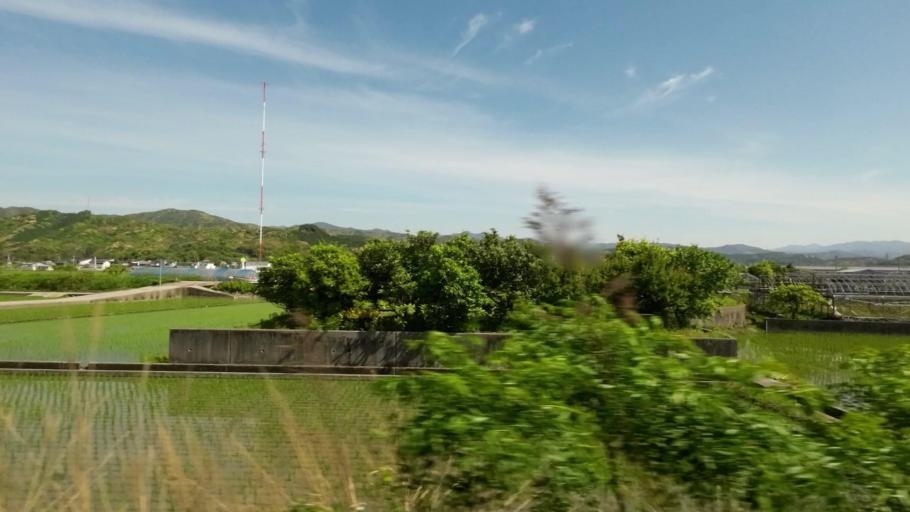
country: JP
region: Kochi
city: Kochi-shi
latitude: 33.5754
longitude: 133.6022
